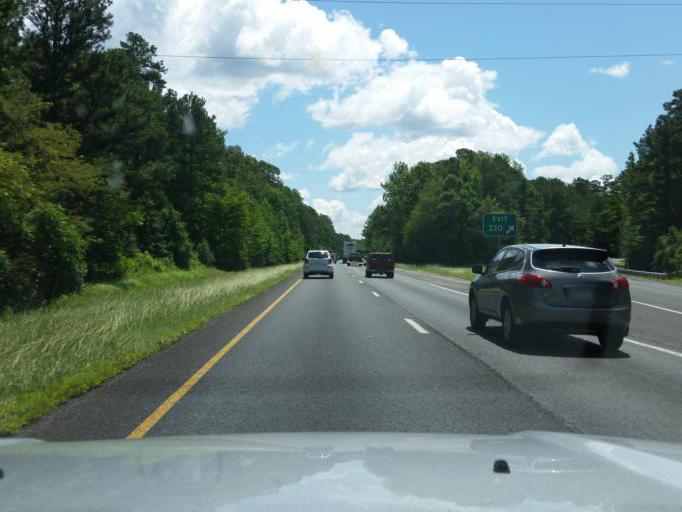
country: US
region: Virginia
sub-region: New Kent County
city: New Kent
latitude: 37.4801
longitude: -76.9261
